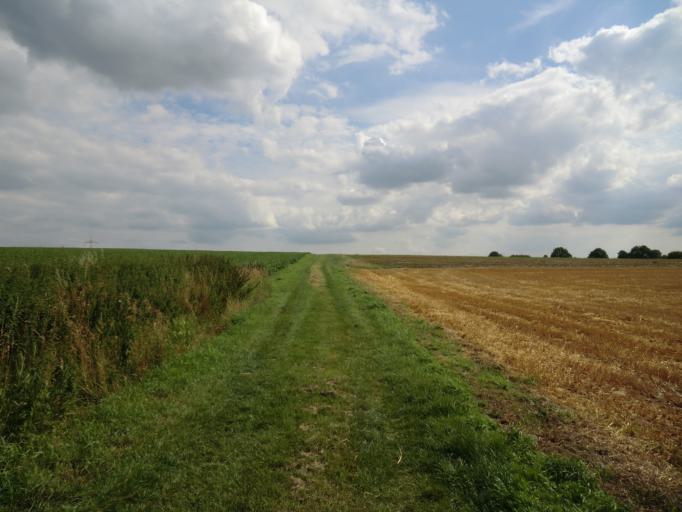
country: DE
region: North Rhine-Westphalia
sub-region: Regierungsbezirk Detmold
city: Hiddenhausen
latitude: 52.1603
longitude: 8.6240
